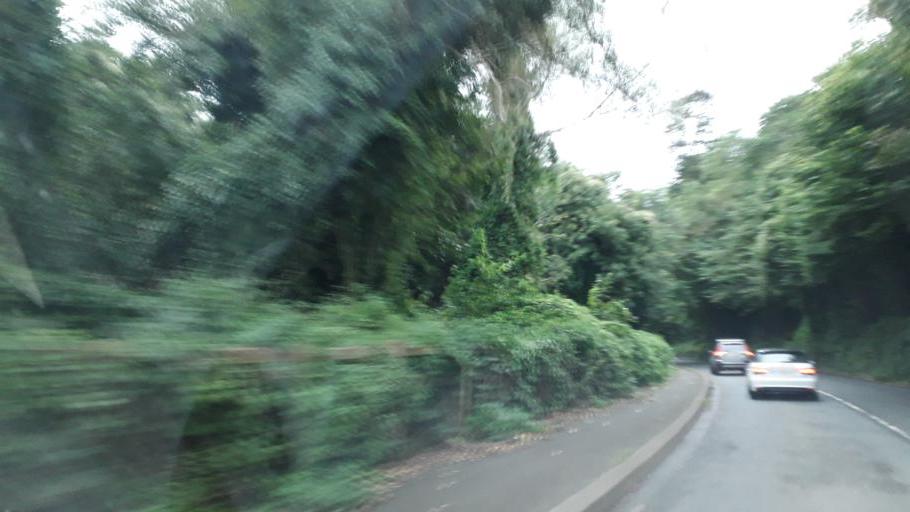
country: IE
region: Leinster
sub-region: Wicklow
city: Enniskerry
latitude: 53.1913
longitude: -6.1581
